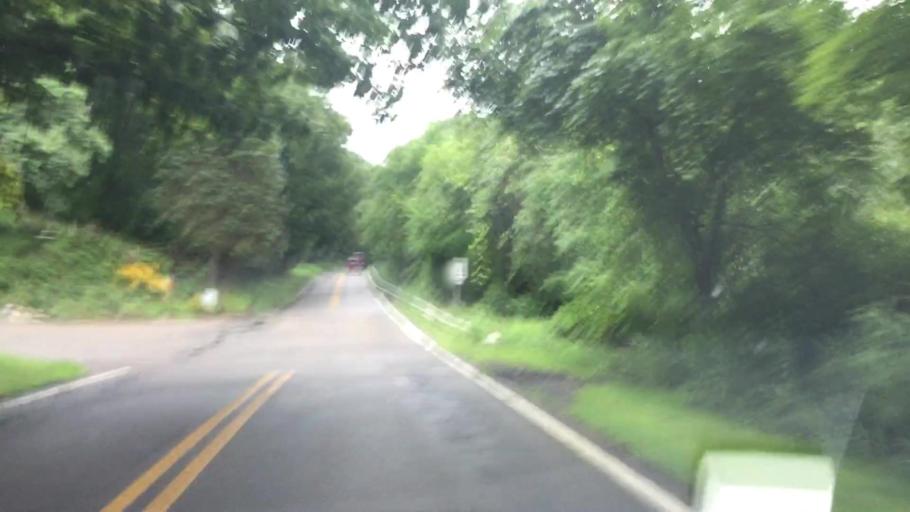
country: US
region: Pennsylvania
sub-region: Allegheny County
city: Bridgeville
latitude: 40.3581
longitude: -80.0981
